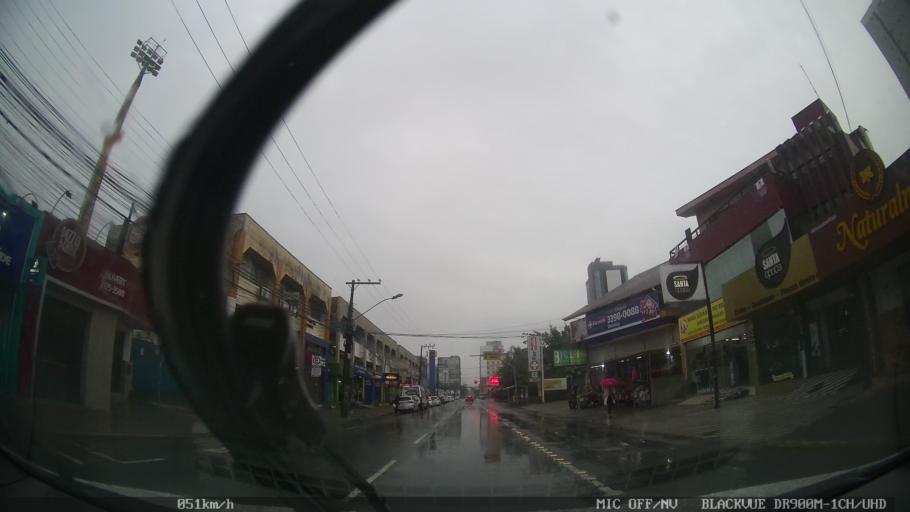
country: BR
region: Santa Catarina
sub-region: Itajai
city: Itajai
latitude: -26.9080
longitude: -48.6588
